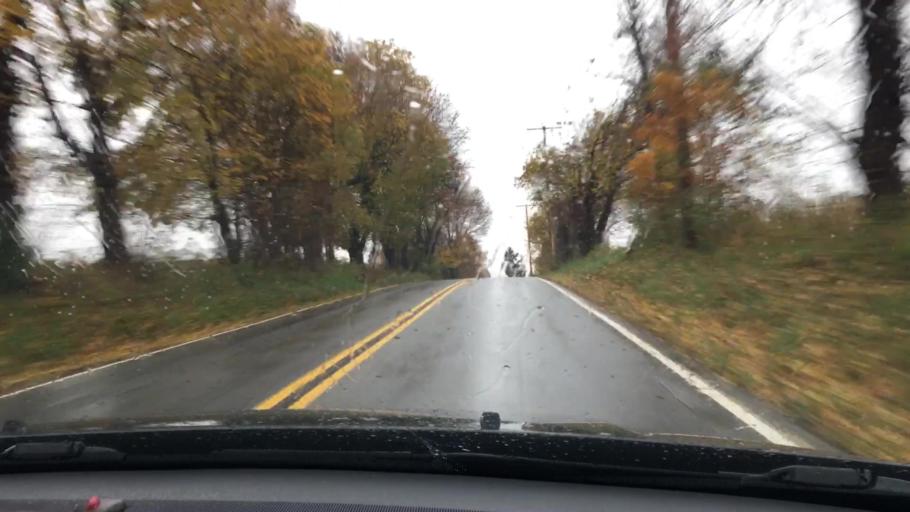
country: US
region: Pennsylvania
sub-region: York County
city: Stewartstown
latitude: 39.7416
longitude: -76.4942
